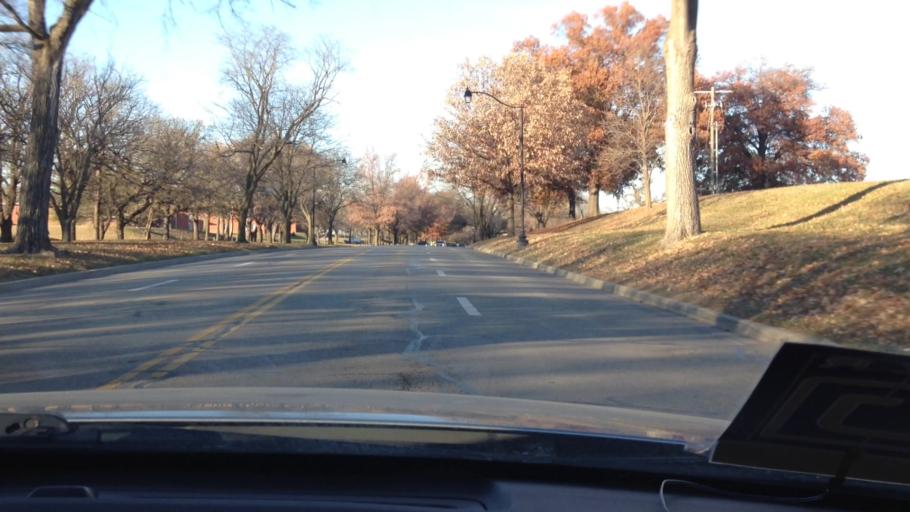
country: US
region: Kansas
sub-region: Leavenworth County
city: Leavenworth
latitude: 39.3397
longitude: -94.9214
